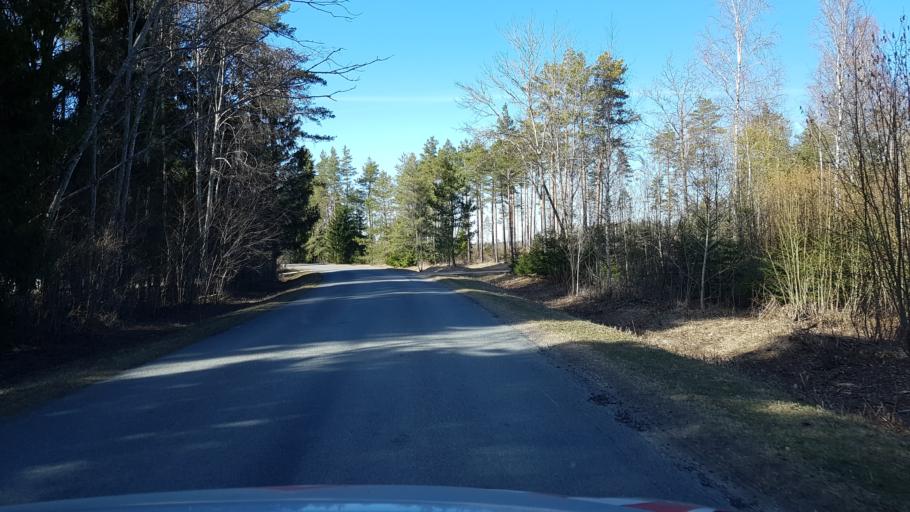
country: EE
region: Harju
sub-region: Nissi vald
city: Riisipere
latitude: 59.0950
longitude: 24.3415
